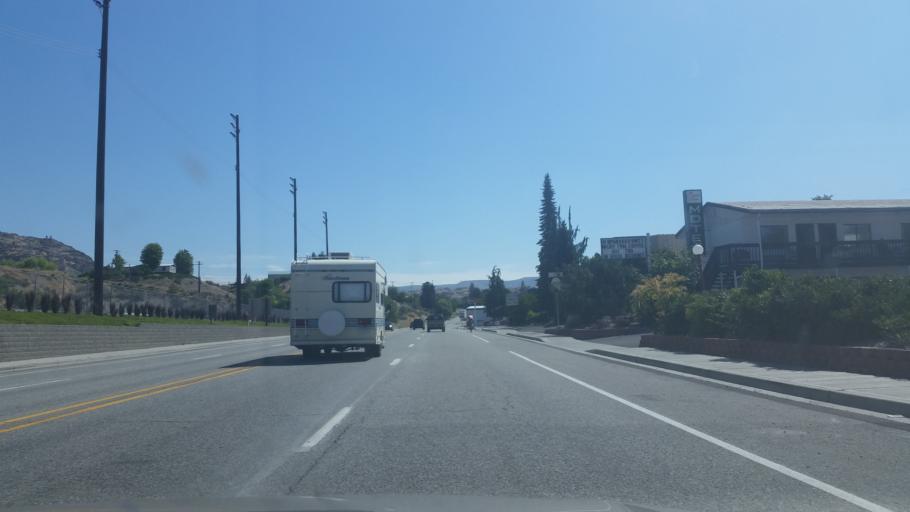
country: US
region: Washington
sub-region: Chelan County
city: Chelan
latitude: 47.8395
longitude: -120.0021
